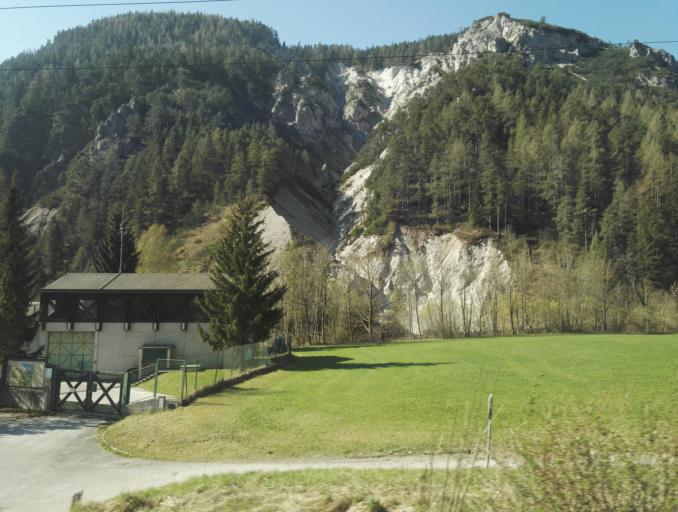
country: AT
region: Salzburg
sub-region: Politischer Bezirk Sankt Johann im Pongau
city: Forstau
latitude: 47.4003
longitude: 13.5822
